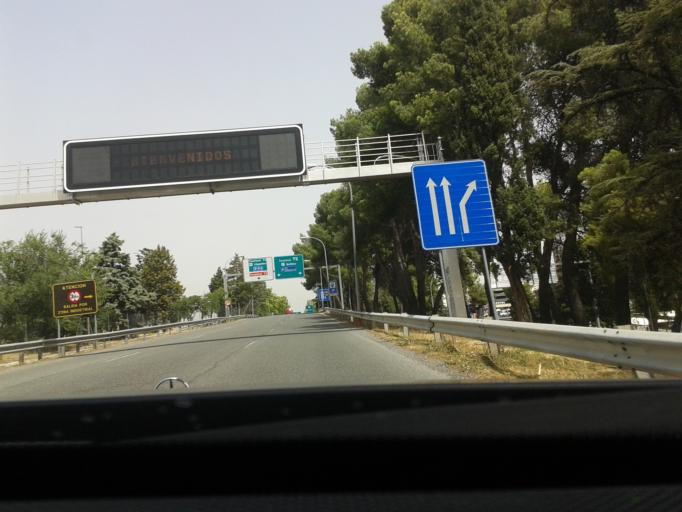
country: ES
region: Madrid
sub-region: Provincia de Madrid
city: Barajas de Madrid
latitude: 40.4642
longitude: -3.5743
